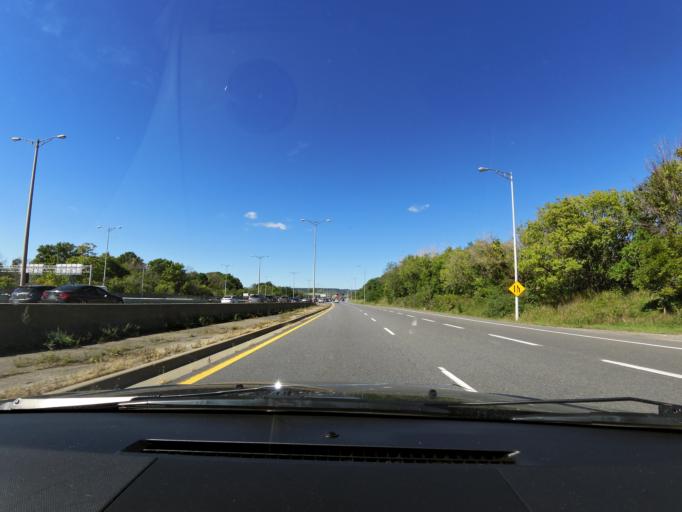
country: CA
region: Ontario
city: Burlington
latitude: 43.3166
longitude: -79.8093
